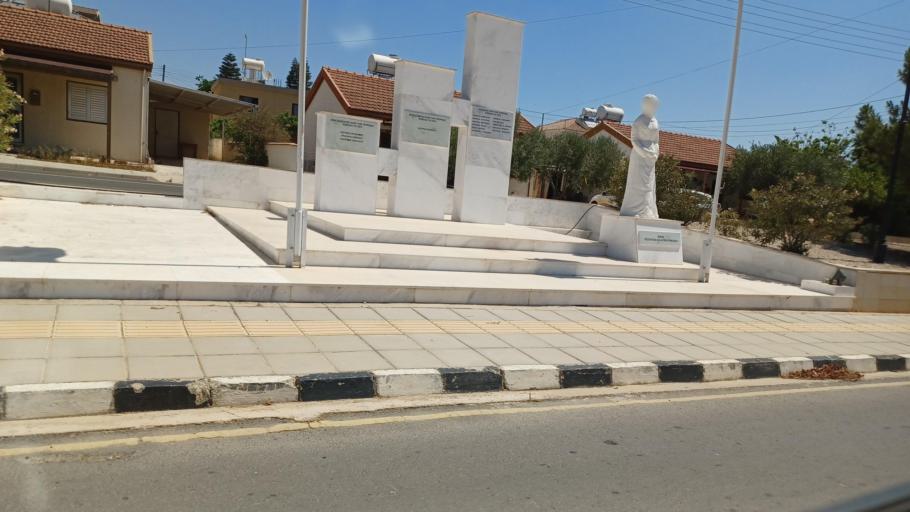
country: CY
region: Ammochostos
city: Acheritou
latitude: 35.0738
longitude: 33.8837
